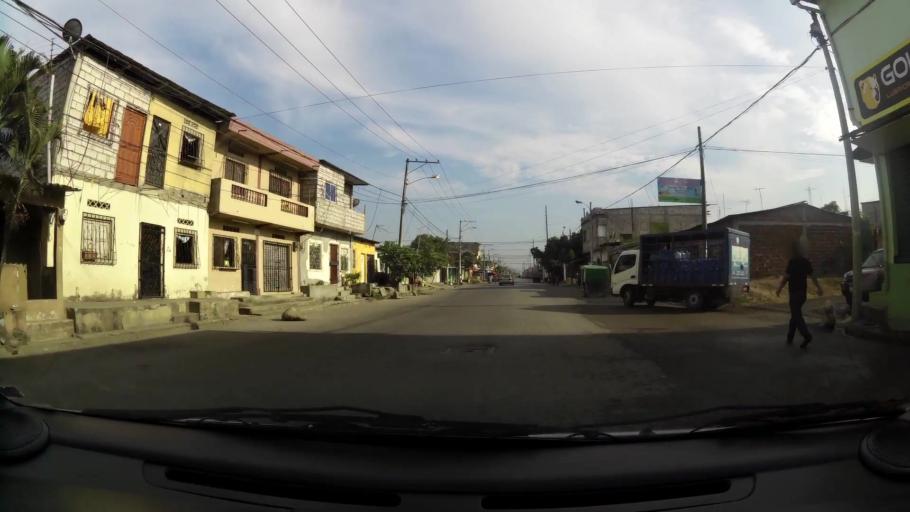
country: EC
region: Guayas
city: Eloy Alfaro
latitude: -2.0778
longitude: -79.9252
